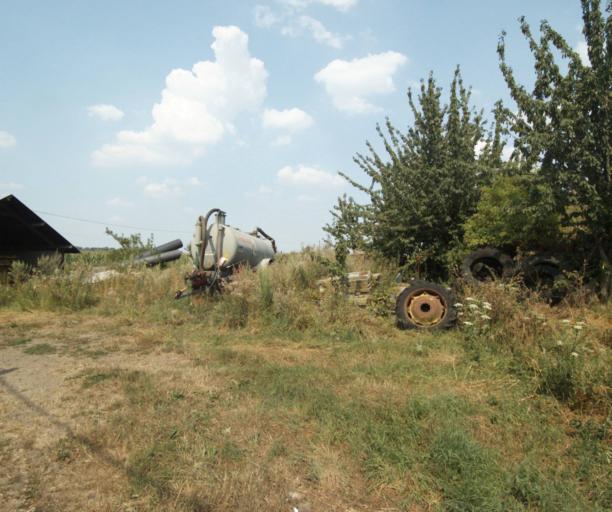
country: FR
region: Nord-Pas-de-Calais
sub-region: Departement du Nord
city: Quesnoy-sur-Deule
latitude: 50.7335
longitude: 3.0026
